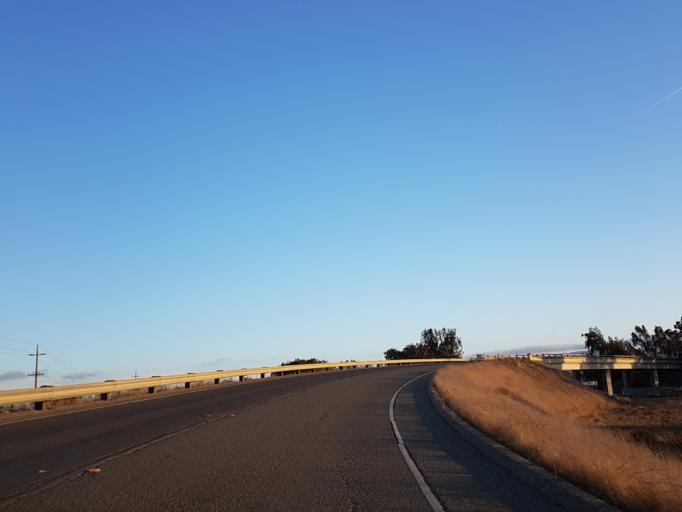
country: US
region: California
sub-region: Monterey County
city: Greenfield
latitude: 36.3407
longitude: -121.2549
